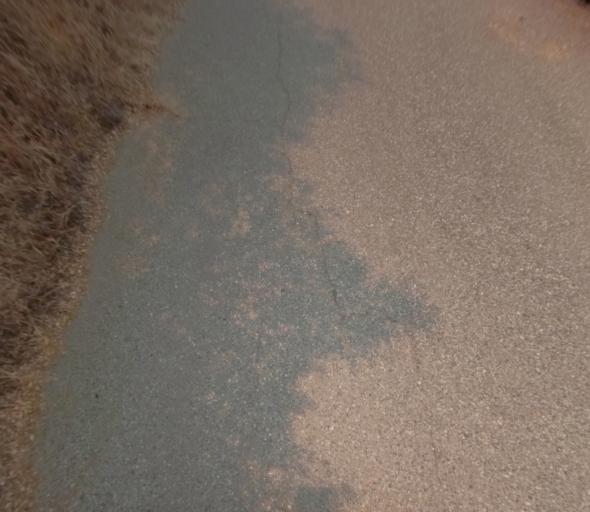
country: US
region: California
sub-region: Madera County
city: Oakhurst
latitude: 37.3165
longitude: -119.5968
